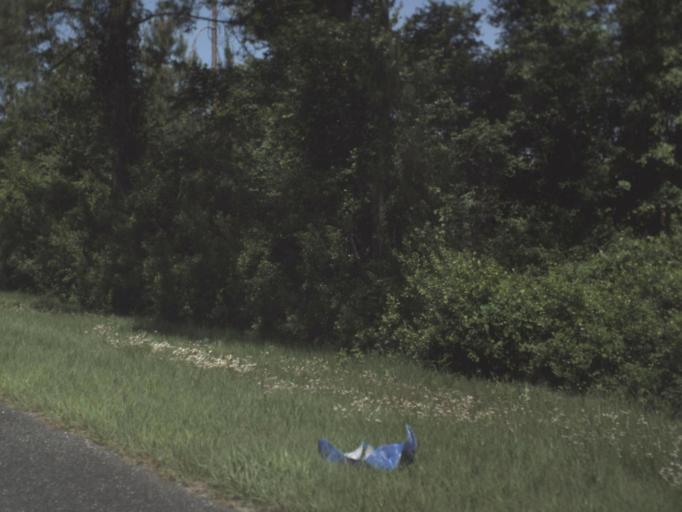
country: US
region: Florida
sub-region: Baker County
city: Macclenny
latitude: 30.2320
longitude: -82.3232
